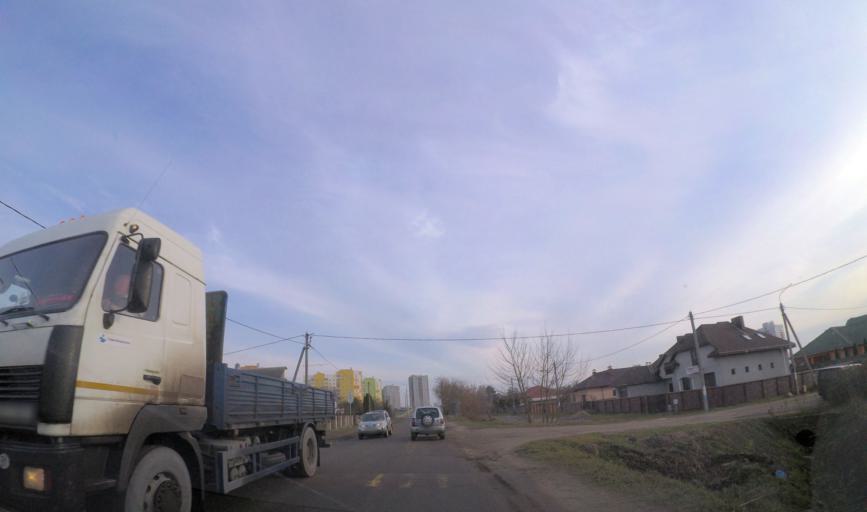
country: BY
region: Grodnenskaya
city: Hrodna
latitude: 53.7186
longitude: 23.8590
